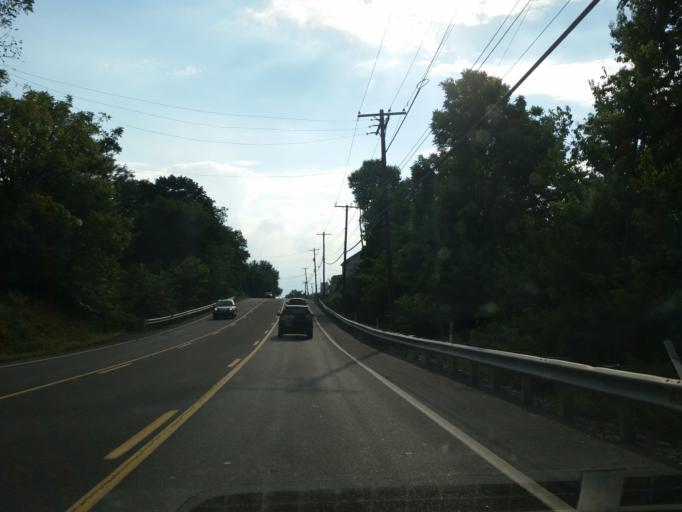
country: US
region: Pennsylvania
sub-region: Lebanon County
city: Annville
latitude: 40.3215
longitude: -76.5541
